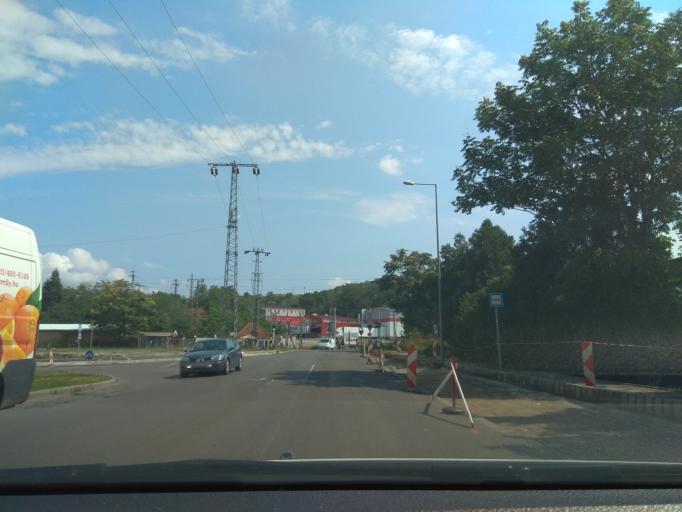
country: HU
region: Heves
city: Eger
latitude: 47.8875
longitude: 20.3955
